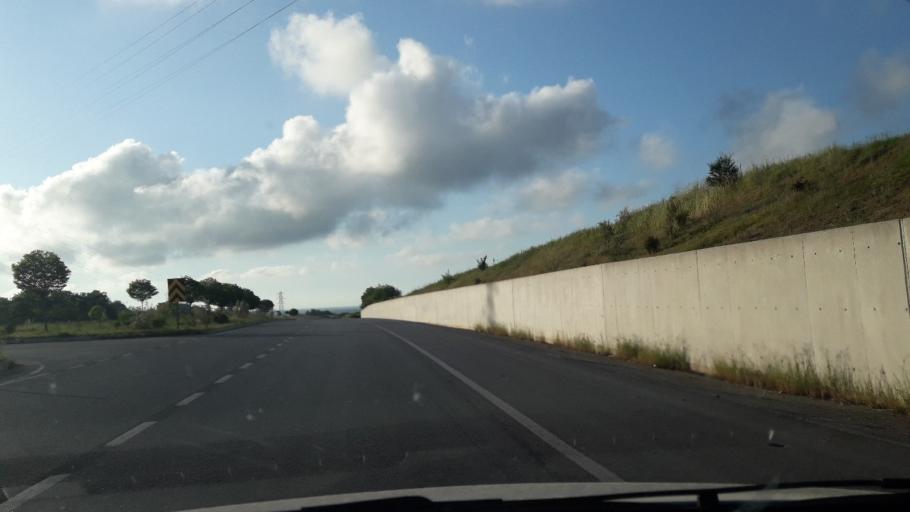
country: TR
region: Samsun
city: Bafra
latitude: 41.5870
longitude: 35.8390
